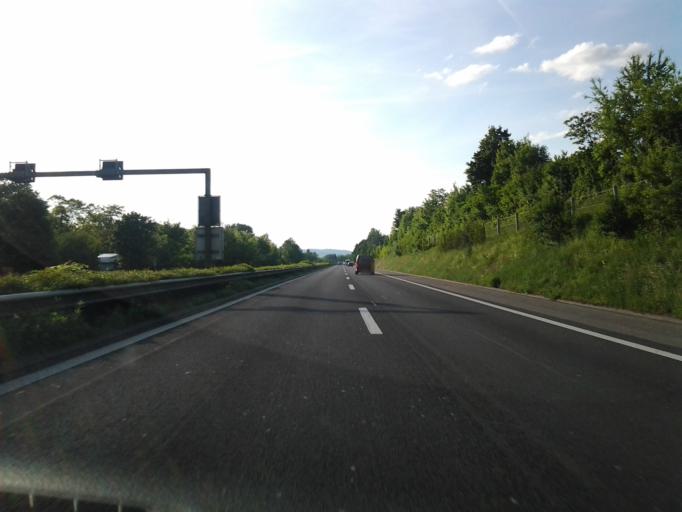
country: CH
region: Lucerne
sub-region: Sursee District
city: Eich
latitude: 47.1552
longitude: 8.1586
